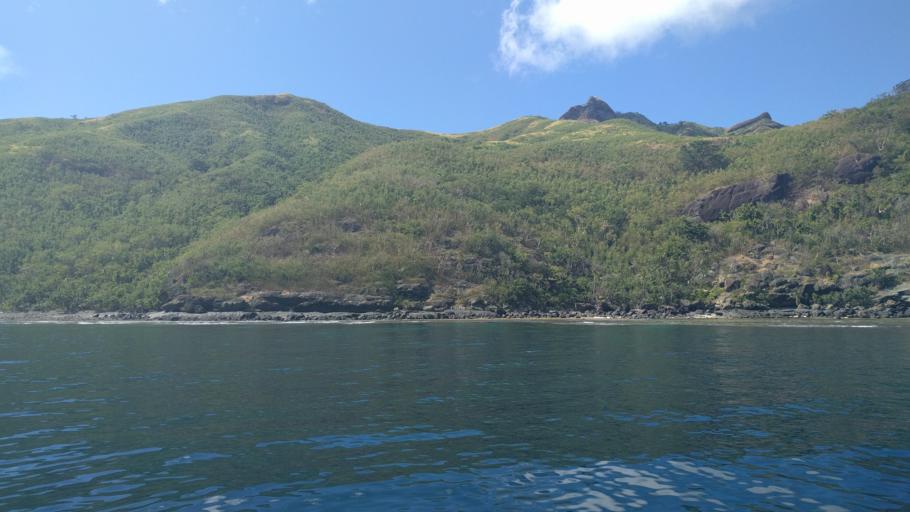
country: FJ
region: Western
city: Lautoka
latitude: -17.2857
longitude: 177.1020
